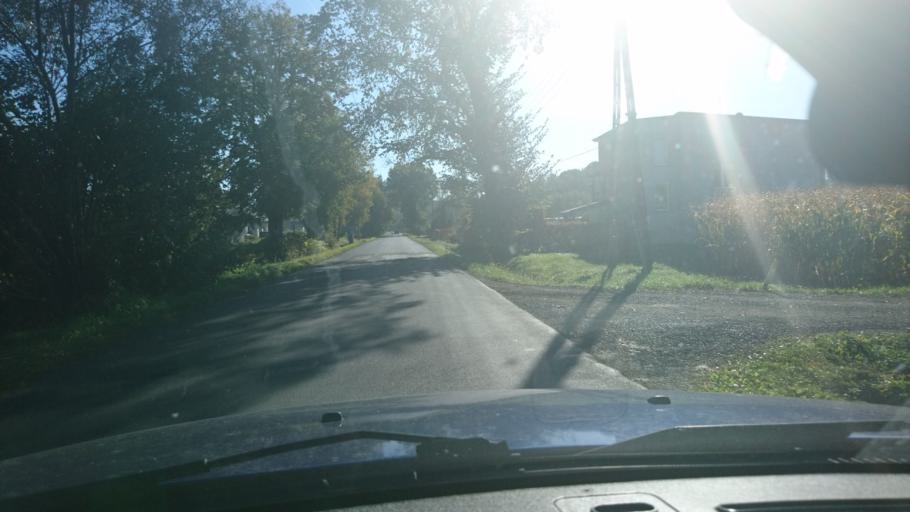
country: PL
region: Silesian Voivodeship
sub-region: Powiat bielski
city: Bronow
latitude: 49.8520
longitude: 18.9369
